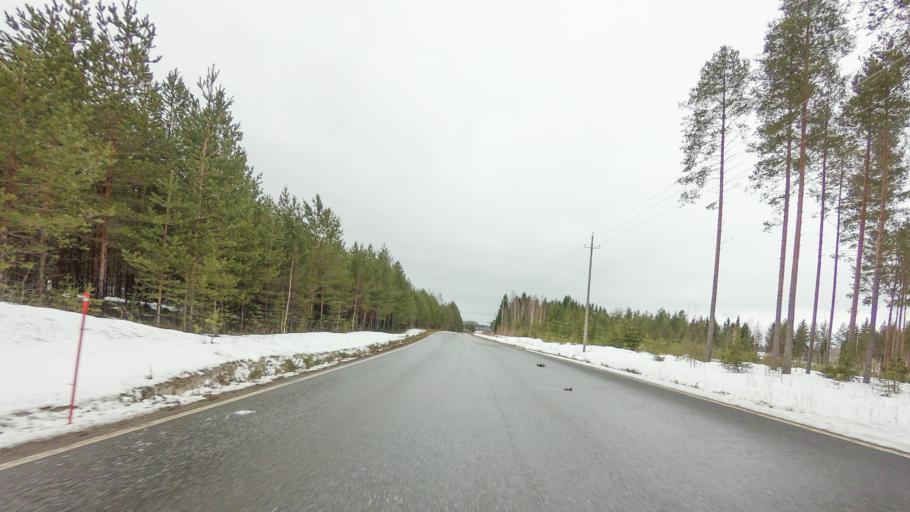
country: FI
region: Southern Savonia
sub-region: Savonlinna
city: Savonlinna
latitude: 61.9658
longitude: 28.8212
